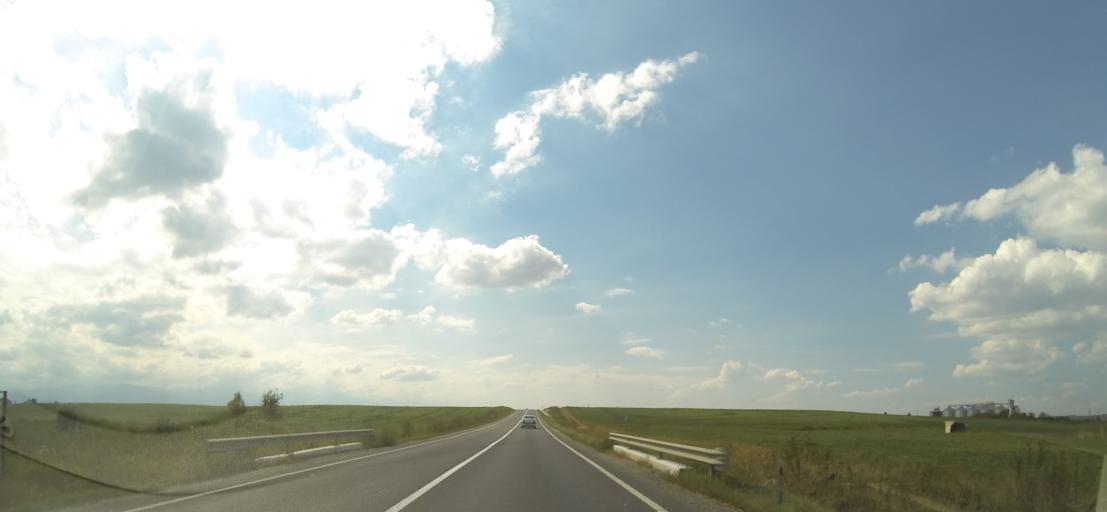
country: RO
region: Brasov
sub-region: Comuna Sercaia
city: Sercaia
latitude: 45.8304
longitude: 25.1230
